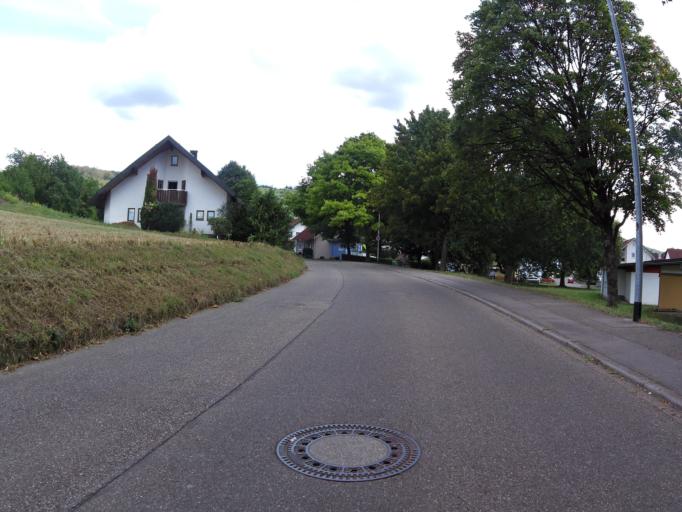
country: DE
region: Baden-Wuerttemberg
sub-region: Freiburg Region
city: Lahr
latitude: 48.3196
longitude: 7.8622
